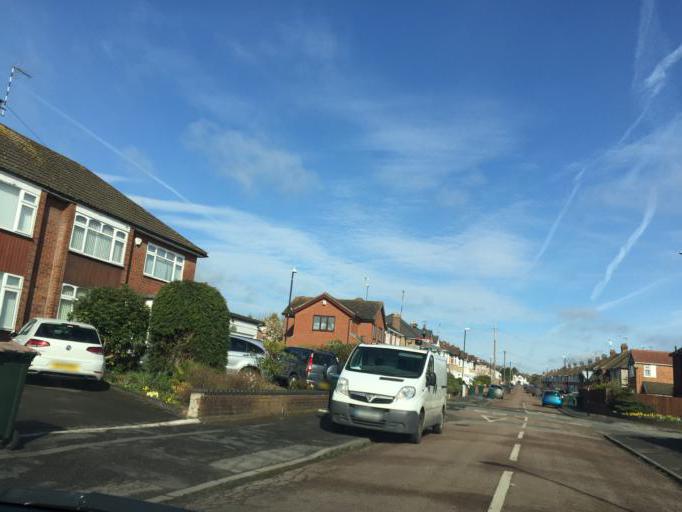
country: GB
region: England
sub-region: Coventry
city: Coventry
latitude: 52.3812
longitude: -1.5082
